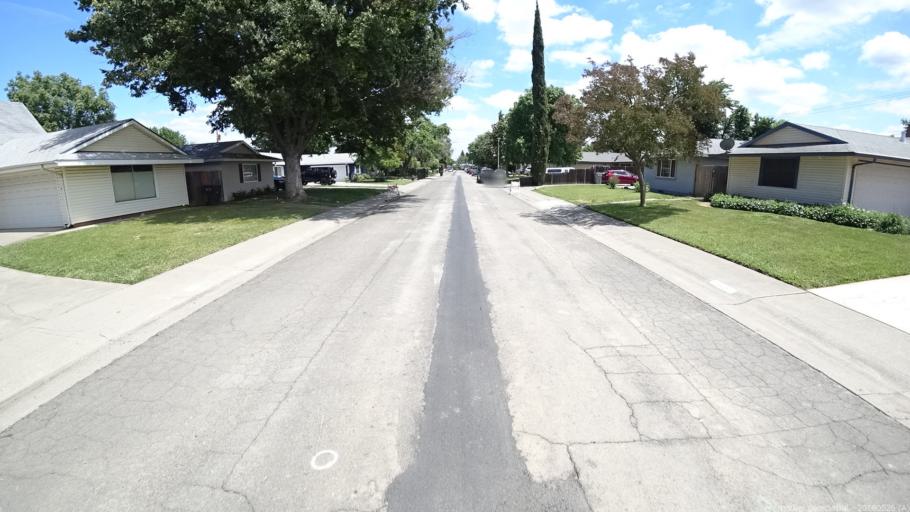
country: US
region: California
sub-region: Sacramento County
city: Sacramento
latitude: 38.6121
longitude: -121.4885
